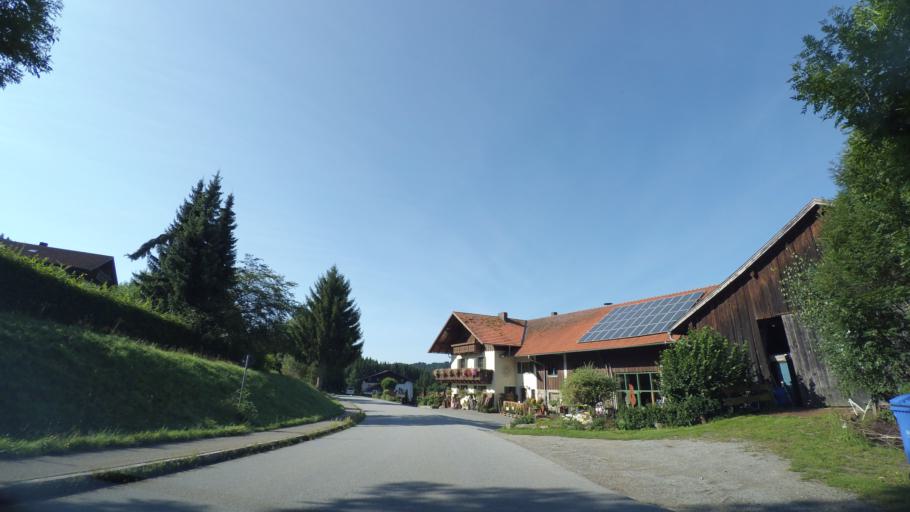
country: DE
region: Bavaria
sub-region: Lower Bavaria
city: Drachselsried
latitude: 49.0959
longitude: 13.0112
